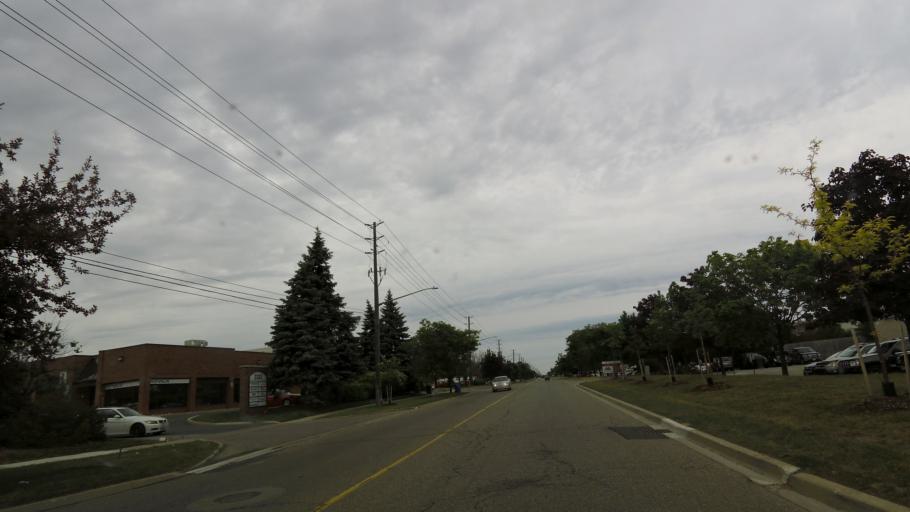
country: CA
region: Ontario
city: Oakville
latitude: 43.4125
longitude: -79.7315
